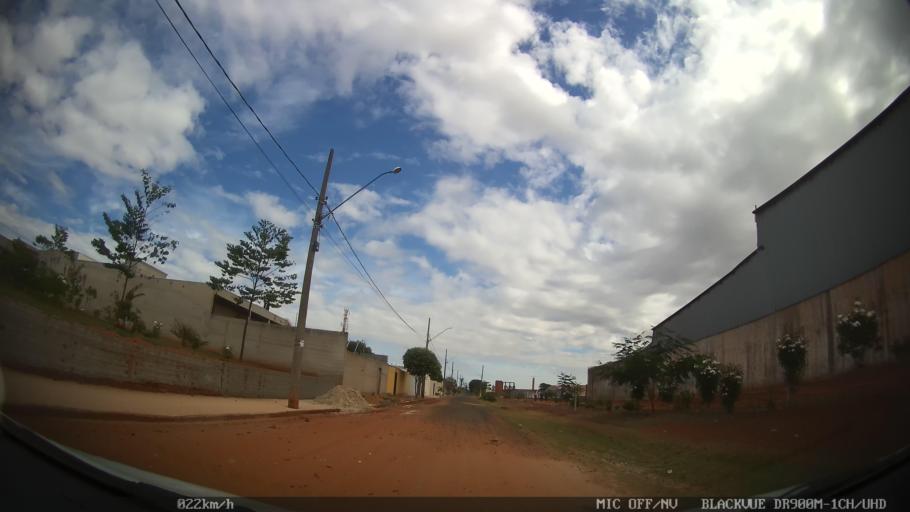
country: BR
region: Sao Paulo
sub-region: Bady Bassitt
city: Bady Bassitt
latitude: -20.8109
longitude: -49.4993
